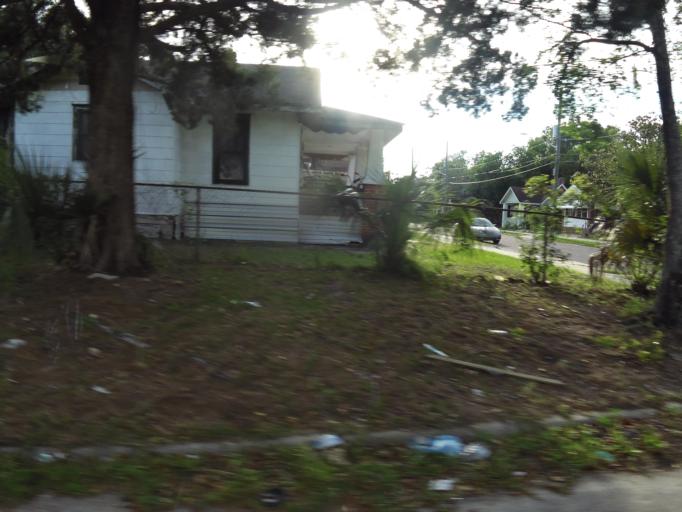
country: US
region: Florida
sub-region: Duval County
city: Jacksonville
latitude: 30.3577
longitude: -81.6555
